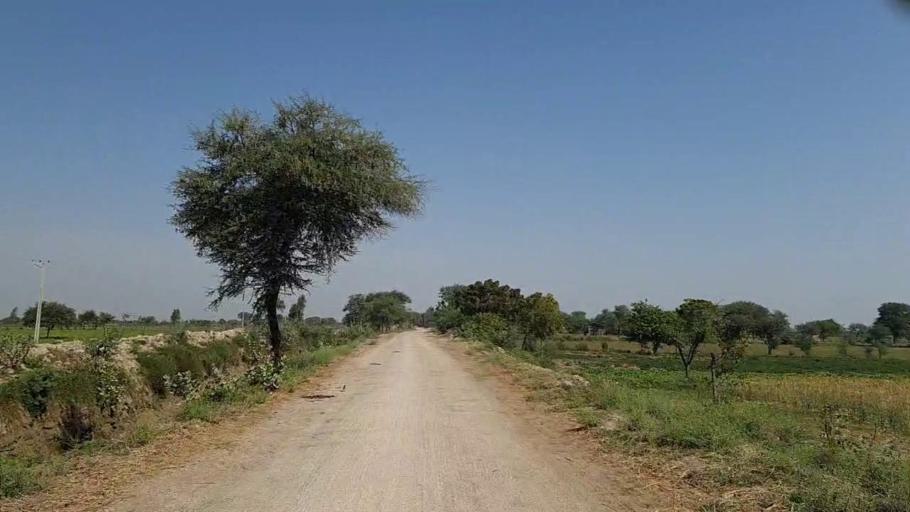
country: PK
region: Sindh
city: Mirpur Batoro
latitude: 24.6962
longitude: 68.2573
